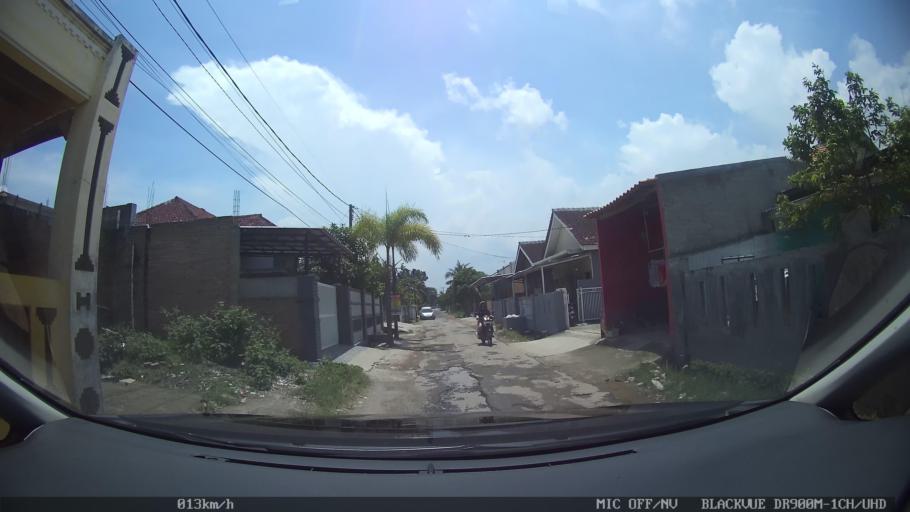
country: ID
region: Lampung
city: Kedaton
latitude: -5.3801
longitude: 105.2941
